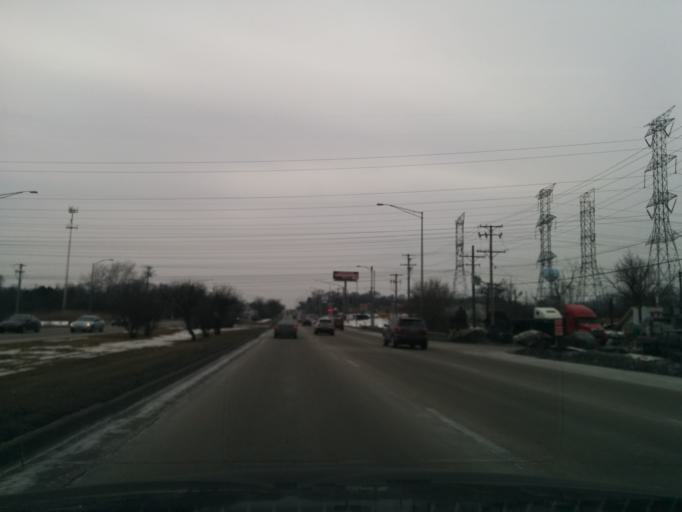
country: US
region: Illinois
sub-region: DuPage County
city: Glendale Heights
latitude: 41.9040
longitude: -88.0470
